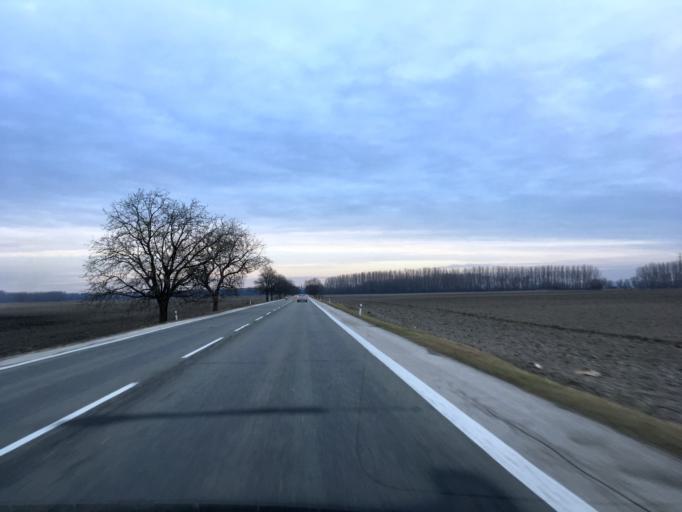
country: SK
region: Trnavsky
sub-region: Okres Dunajska Streda
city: Velky Meder
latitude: 47.9143
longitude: 17.7296
